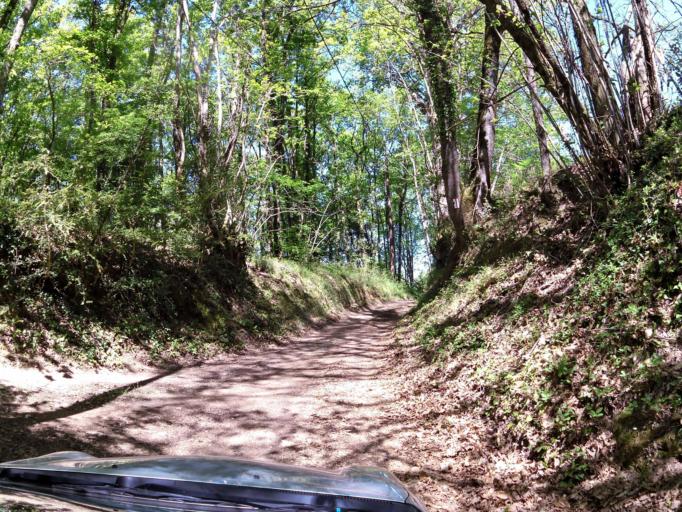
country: FR
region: Aquitaine
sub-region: Departement de la Dordogne
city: Domme
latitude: 44.7900
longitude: 1.2191
